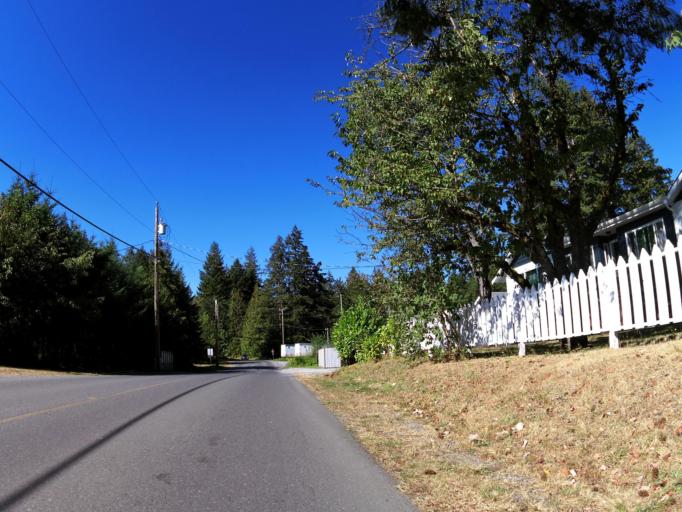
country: CA
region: British Columbia
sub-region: Cowichan Valley Regional District
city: Ladysmith
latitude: 49.0417
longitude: -123.8510
